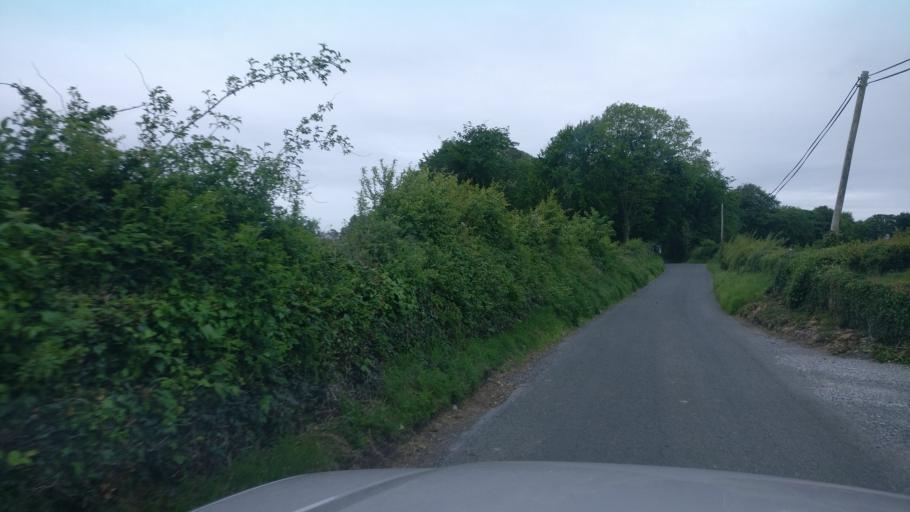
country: IE
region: Connaught
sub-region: County Galway
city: Loughrea
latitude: 53.1139
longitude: -8.4161
